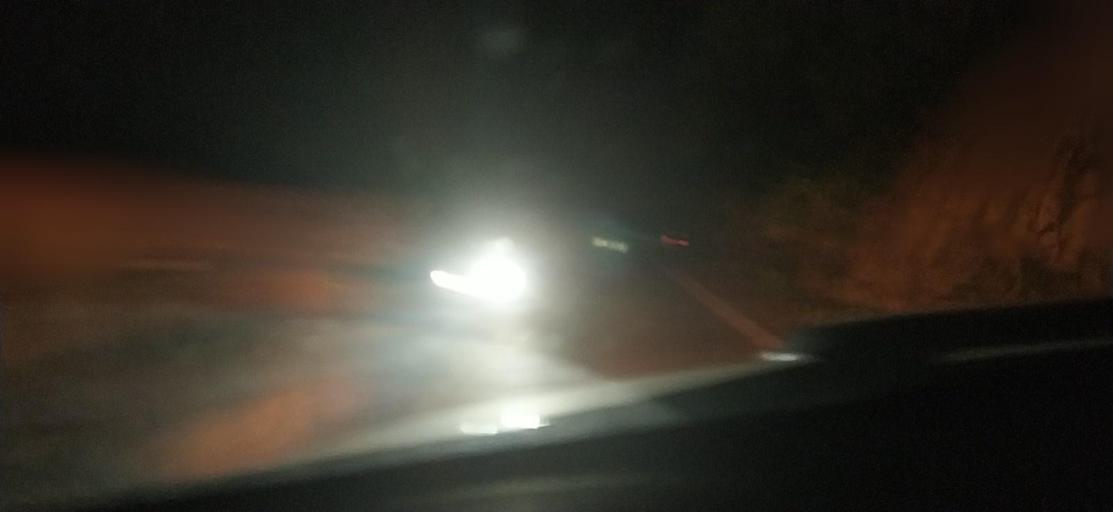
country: BR
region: Minas Gerais
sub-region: Mato Verde
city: Mato Verde
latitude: -15.5330
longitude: -42.9217
